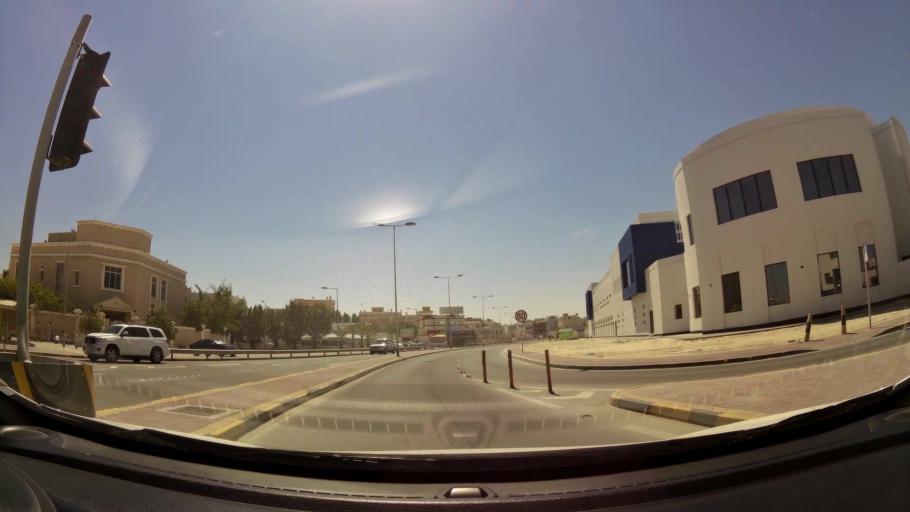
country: BH
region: Muharraq
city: Al Muharraq
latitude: 26.2715
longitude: 50.6041
